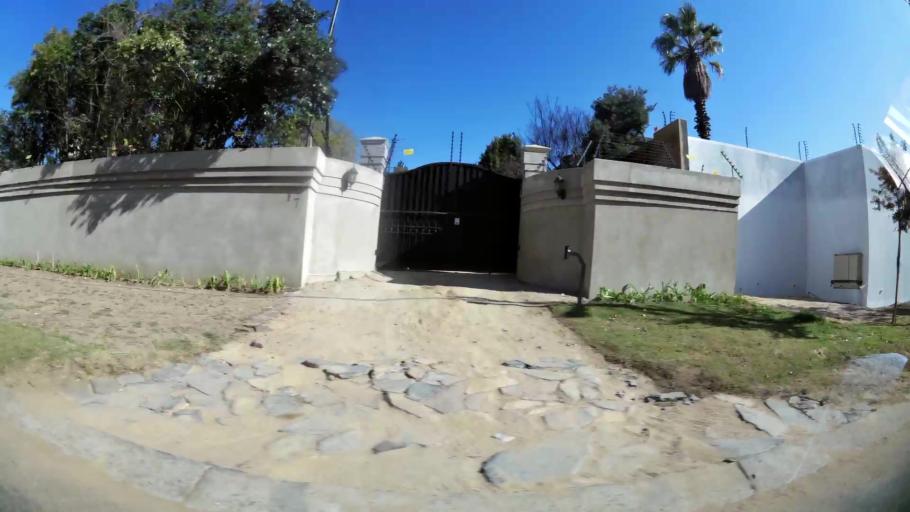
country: ZA
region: Gauteng
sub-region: City of Johannesburg Metropolitan Municipality
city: Midrand
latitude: -26.0627
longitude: 28.0399
